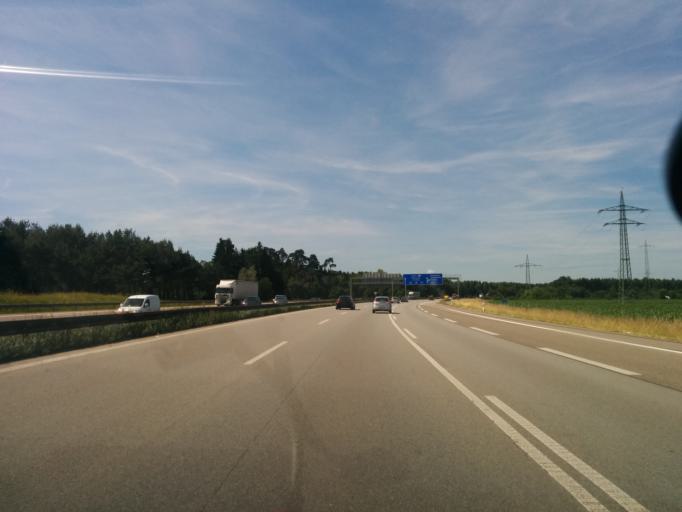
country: DE
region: Bavaria
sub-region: Upper Bavaria
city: Krailling
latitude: 48.1219
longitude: 11.3999
